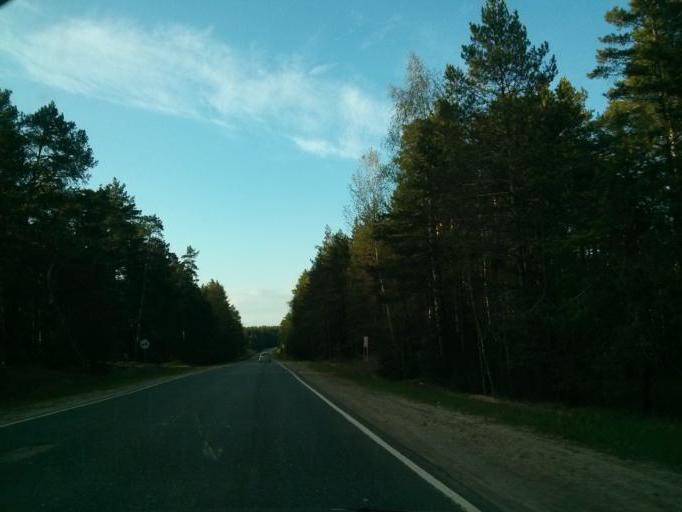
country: RU
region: Nizjnij Novgorod
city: Navashino
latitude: 55.6594
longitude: 42.2581
